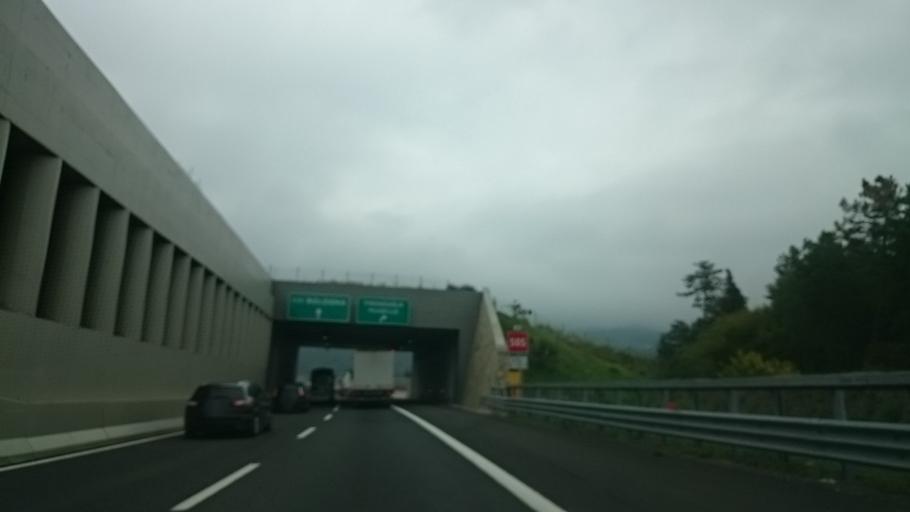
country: IT
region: Tuscany
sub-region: Province of Florence
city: Barberino di Mugello
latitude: 44.0632
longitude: 11.2446
